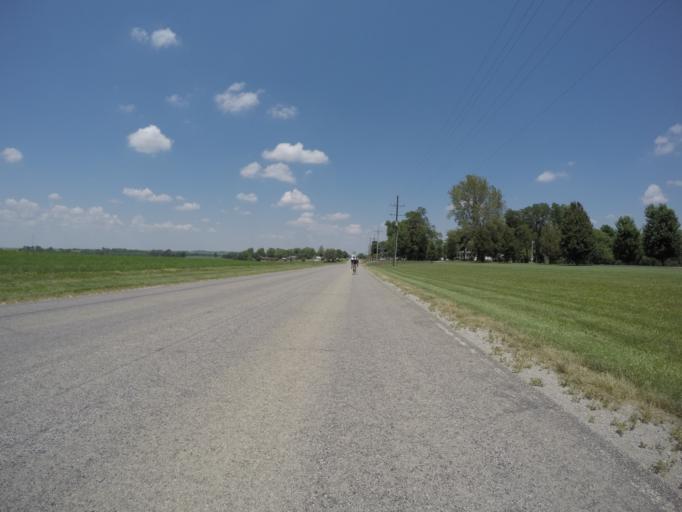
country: US
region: Kansas
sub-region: Doniphan County
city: Troy
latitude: 39.7768
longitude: -95.0970
